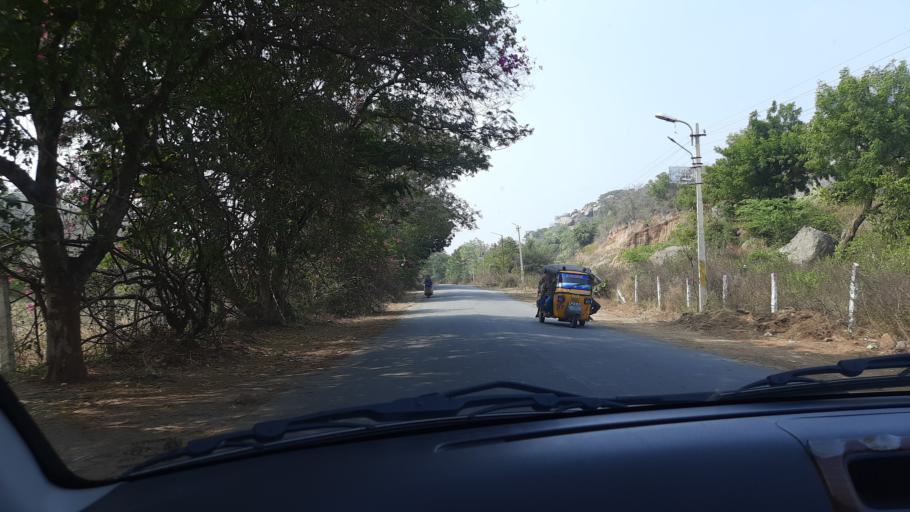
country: IN
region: Telangana
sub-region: Rangareddi
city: Lal Bahadur Nagar
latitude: 17.2751
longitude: 78.6659
